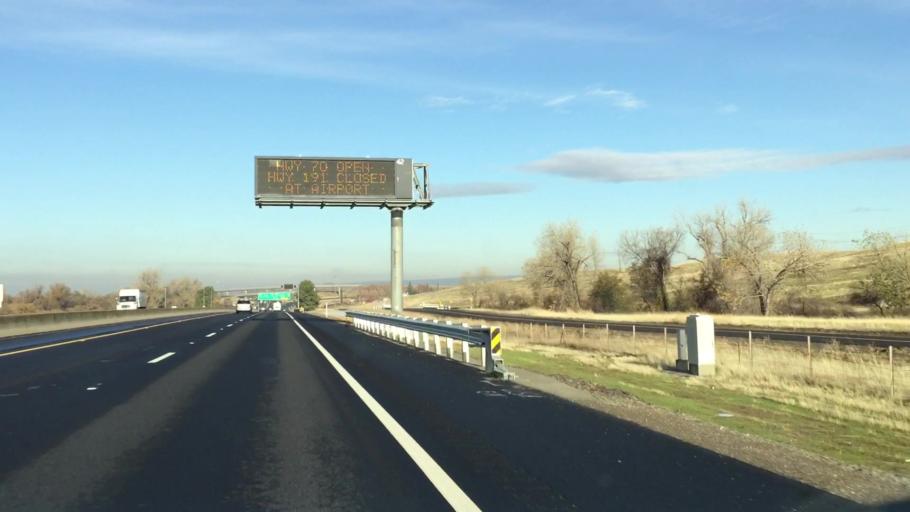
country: US
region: California
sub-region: Butte County
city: Thermalito
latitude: 39.5721
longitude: -121.6139
